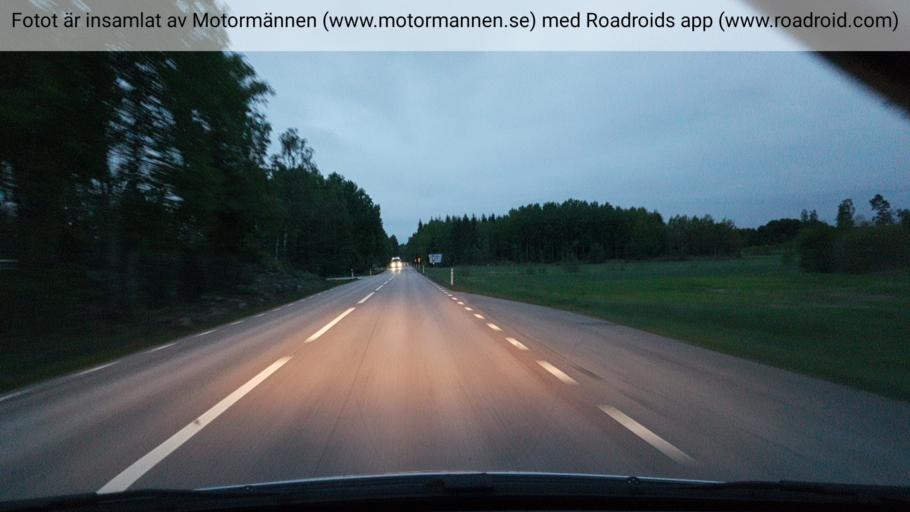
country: SE
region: Uppsala
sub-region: Heby Kommun
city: Heby
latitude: 59.8121
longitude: 16.7854
